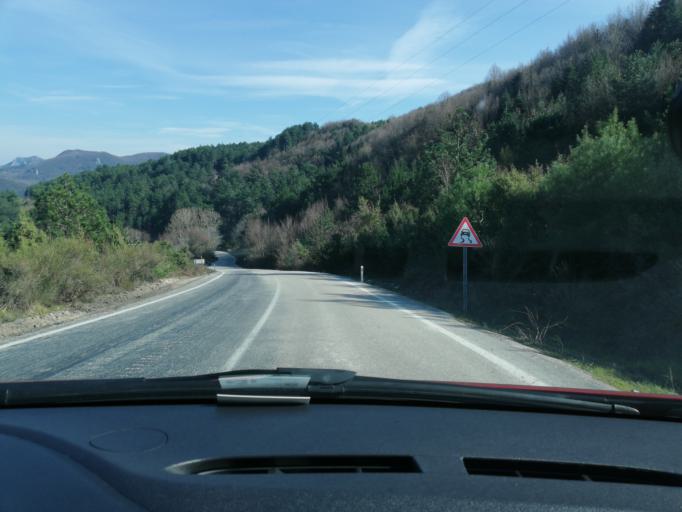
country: TR
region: Bartin
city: Kurucasile
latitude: 41.8336
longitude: 32.6954
